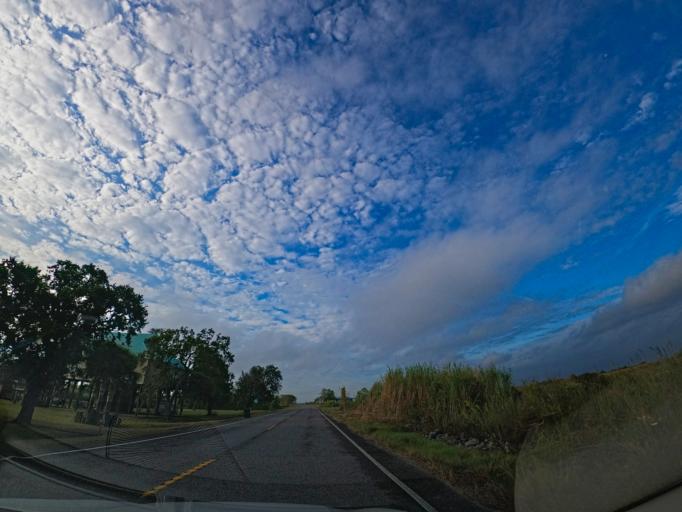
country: US
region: Louisiana
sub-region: Terrebonne Parish
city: Chauvin
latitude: 29.3685
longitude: -90.6250
